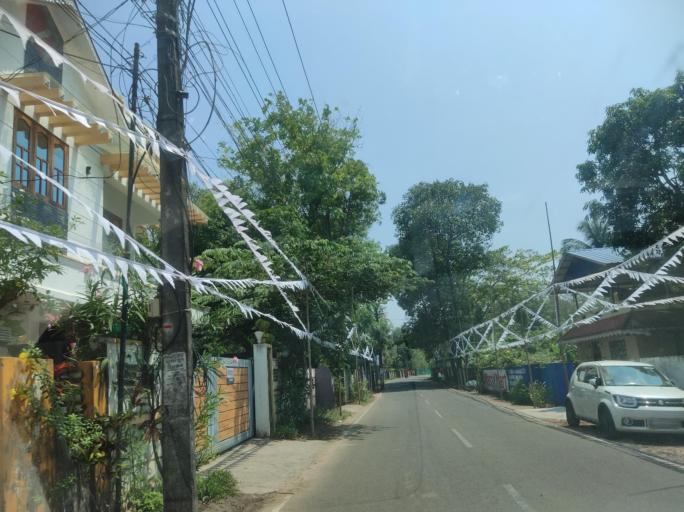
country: IN
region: Kerala
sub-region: Alappuzha
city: Kutiatodu
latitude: 9.7997
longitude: 76.3018
